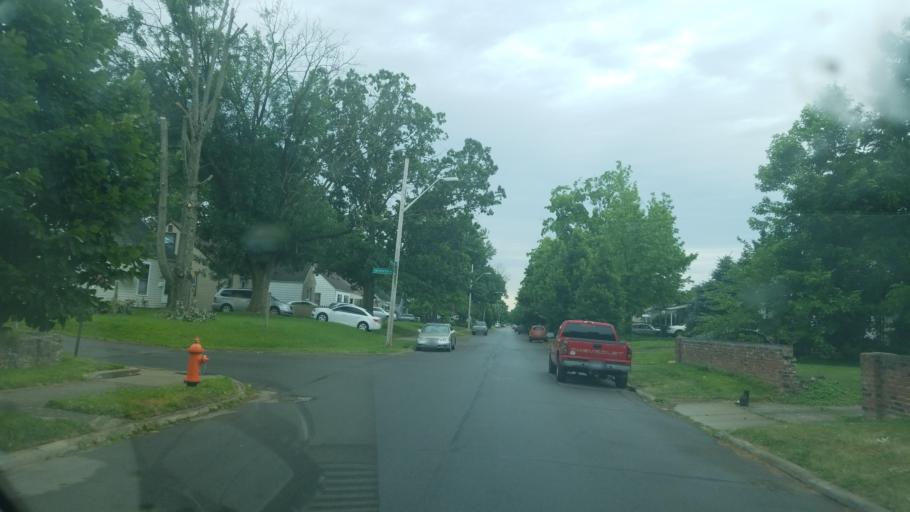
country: US
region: Ohio
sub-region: Franklin County
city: Columbus
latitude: 40.0218
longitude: -82.9851
